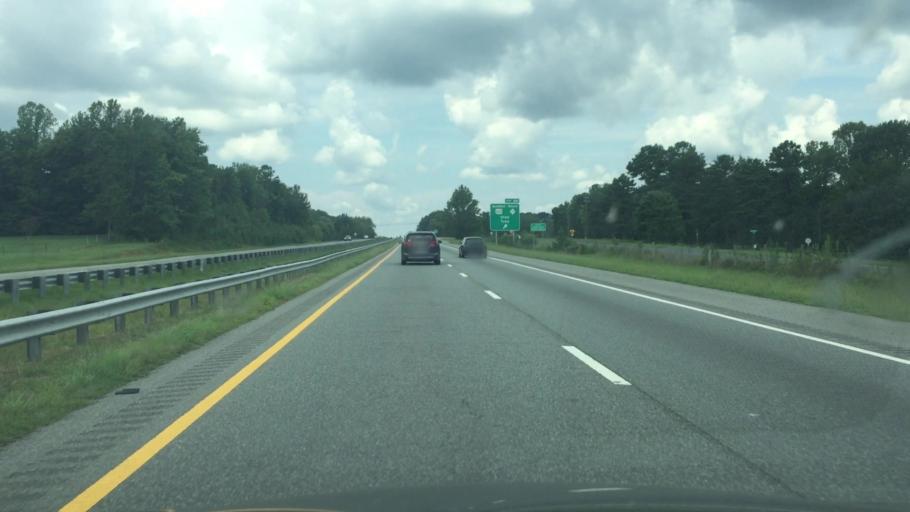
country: US
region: North Carolina
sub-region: Randolph County
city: Asheboro
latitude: 35.6159
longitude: -79.8218
